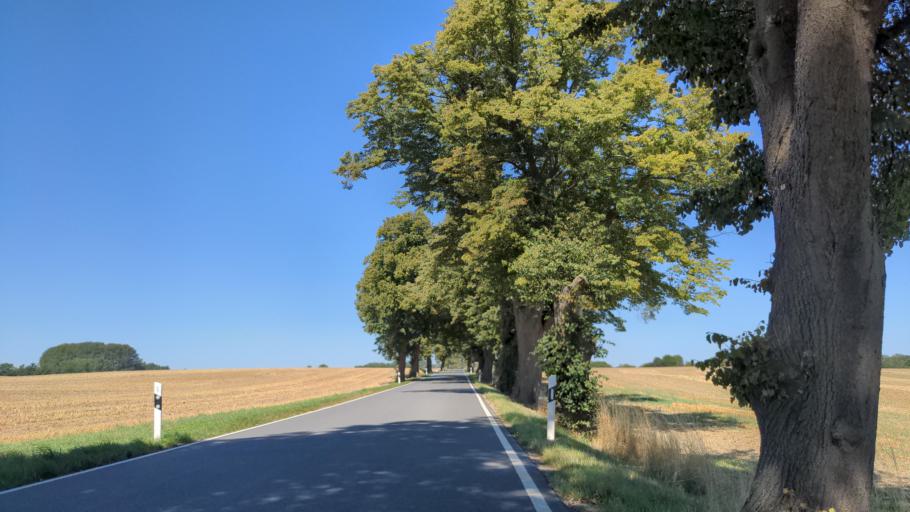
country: DE
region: Mecklenburg-Vorpommern
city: Klutz
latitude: 53.9855
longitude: 11.1329
